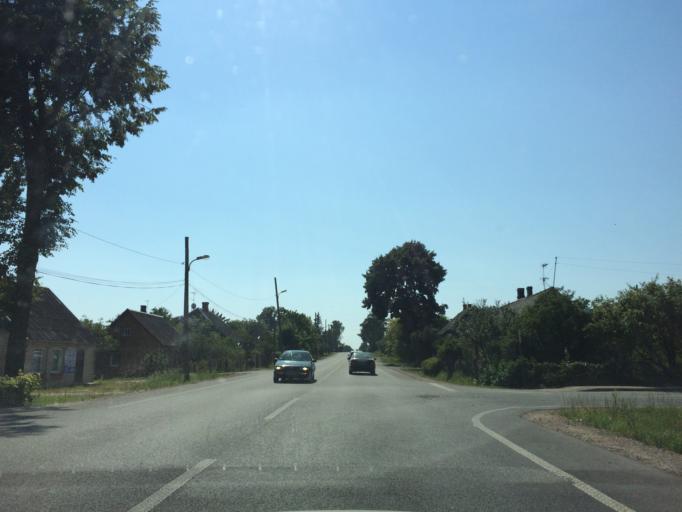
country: LV
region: Rezekne
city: Rezekne
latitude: 56.3500
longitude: 27.1697
